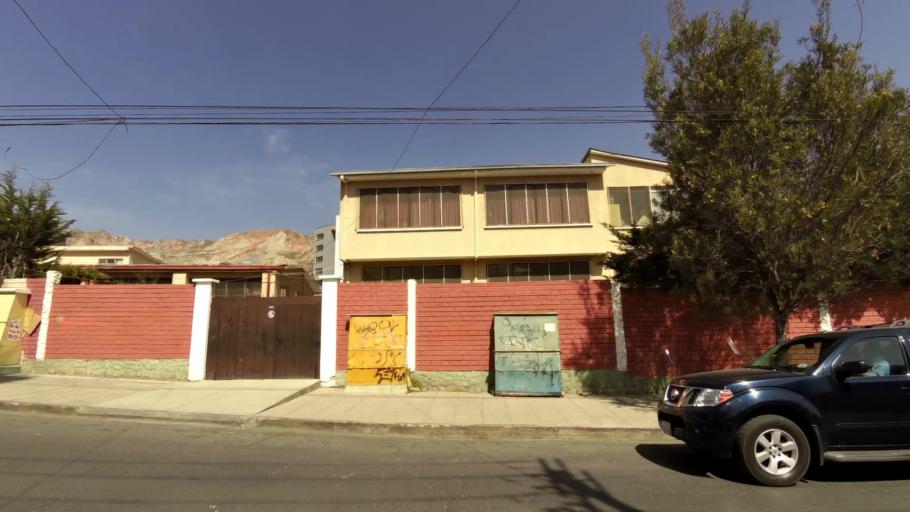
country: BO
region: La Paz
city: La Paz
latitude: -16.5454
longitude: -68.0788
